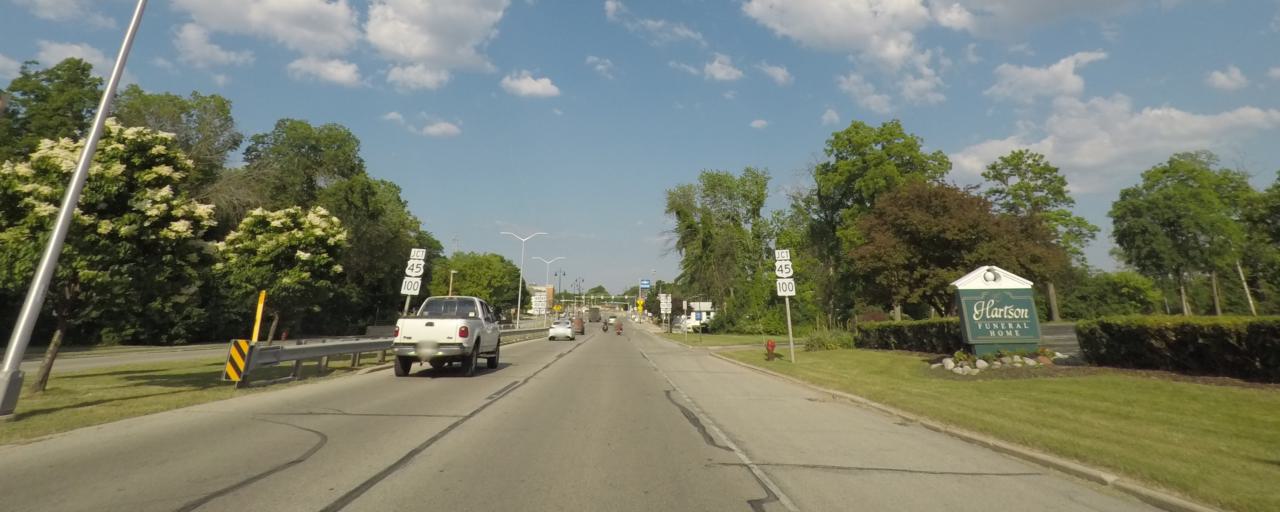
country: US
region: Wisconsin
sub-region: Milwaukee County
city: Hales Corners
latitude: 42.9372
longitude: -88.0526
